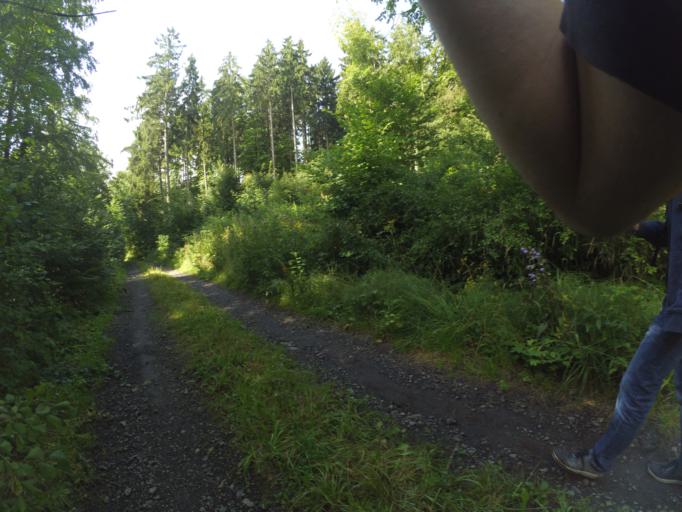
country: DE
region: Hesse
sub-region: Regierungsbezirk Kassel
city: Kirchheim
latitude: 50.8837
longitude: 9.5277
